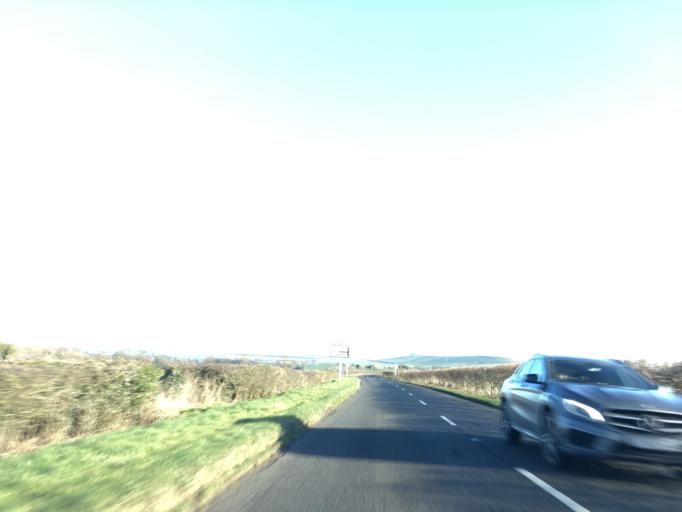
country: GB
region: England
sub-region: Borough of Swindon
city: Chiseldon
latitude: 51.5187
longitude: -1.7519
